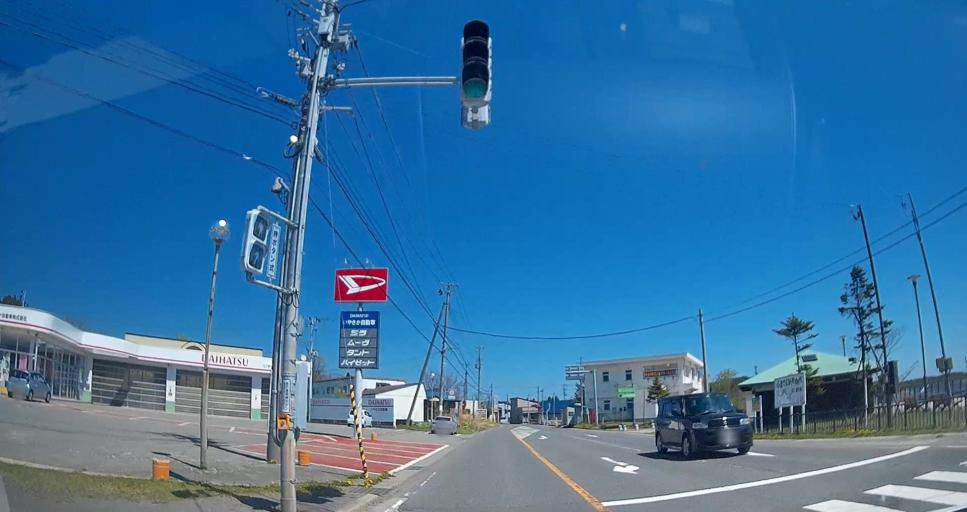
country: JP
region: Aomori
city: Misawa
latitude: 40.9601
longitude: 141.3726
